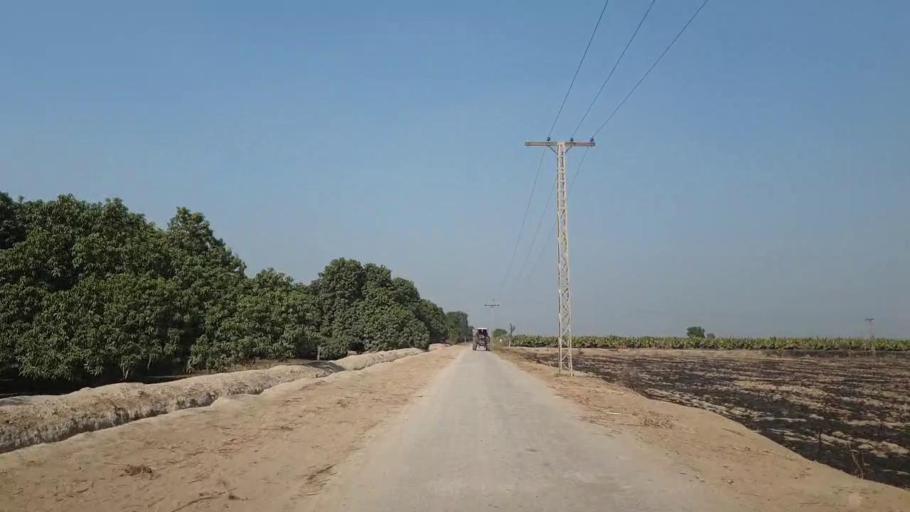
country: PK
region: Sindh
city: Tando Allahyar
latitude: 25.5020
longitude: 68.8221
